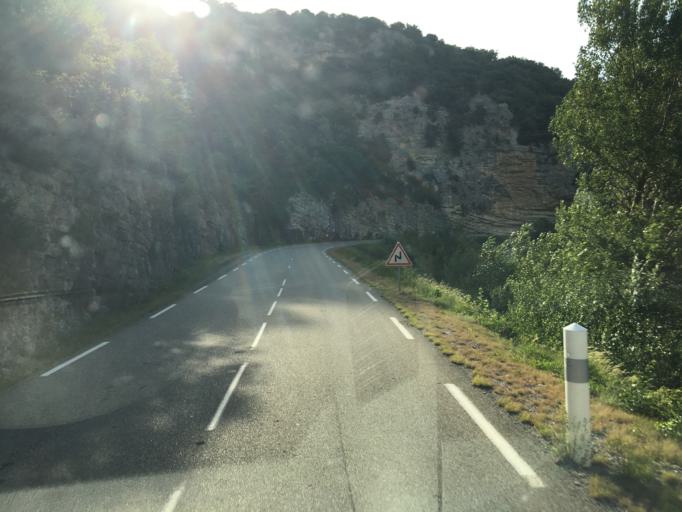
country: FR
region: Rhone-Alpes
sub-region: Departement de la Drome
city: Buis-les-Baronnies
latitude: 44.4315
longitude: 5.2992
